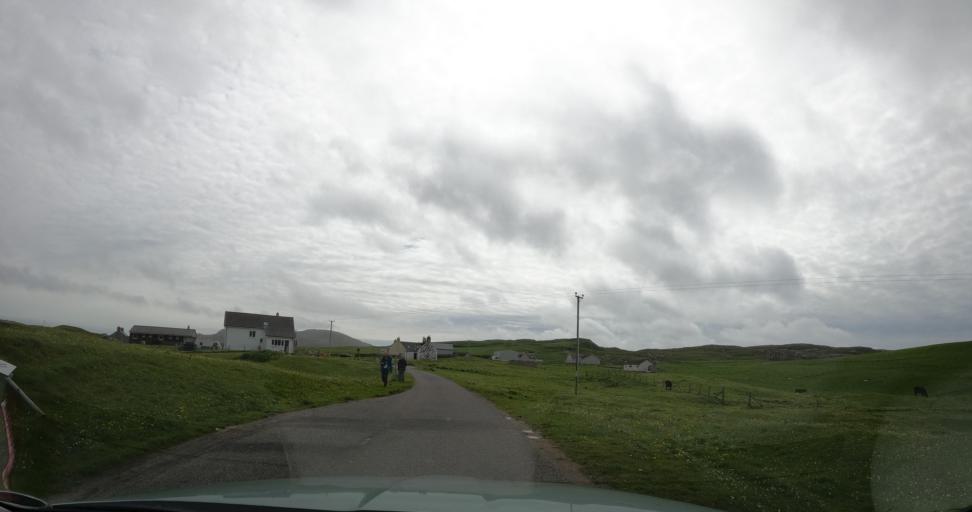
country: GB
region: Scotland
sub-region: Eilean Siar
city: Barra
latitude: 56.9201
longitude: -7.5380
